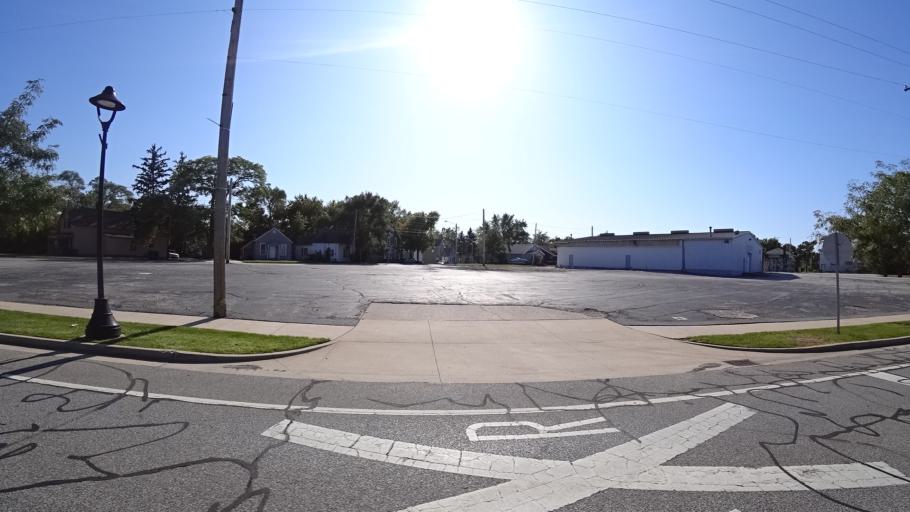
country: US
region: Indiana
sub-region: LaPorte County
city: Michigan City
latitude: 41.7135
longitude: -86.8878
